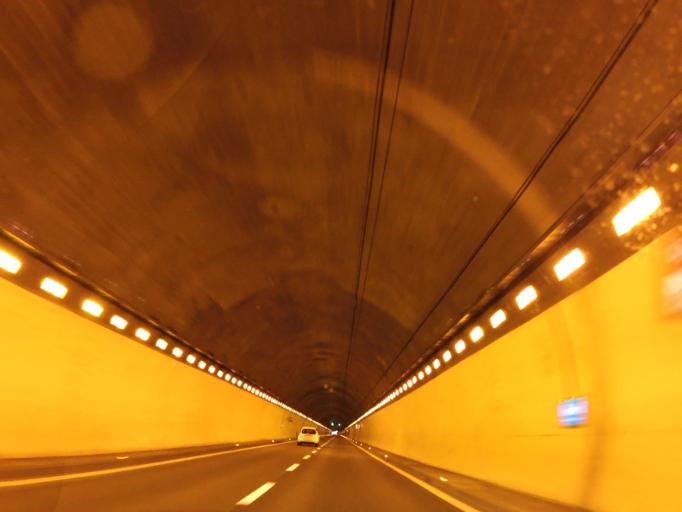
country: IT
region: Trentino-Alto Adige
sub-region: Bolzano
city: Cornaiano
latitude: 46.4788
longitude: 11.3064
